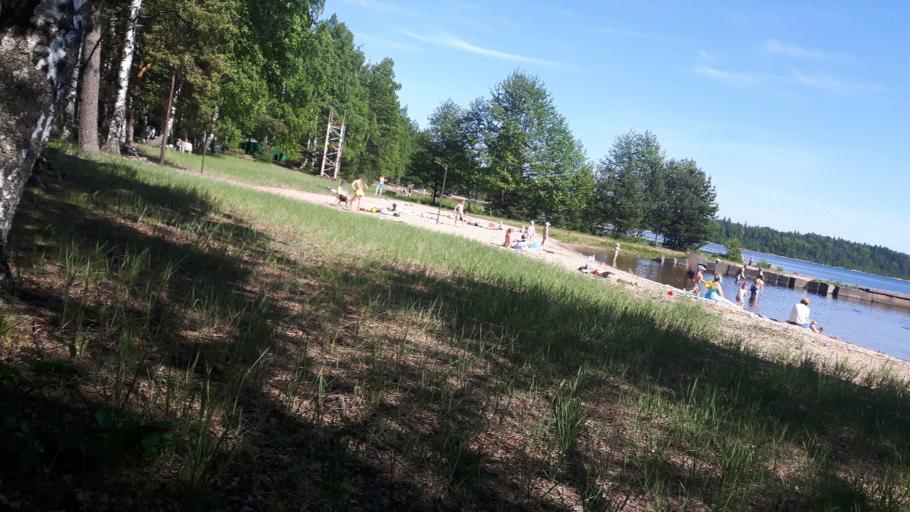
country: RU
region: Leningrad
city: Sista-Palkino
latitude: 59.7614
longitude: 28.7401
